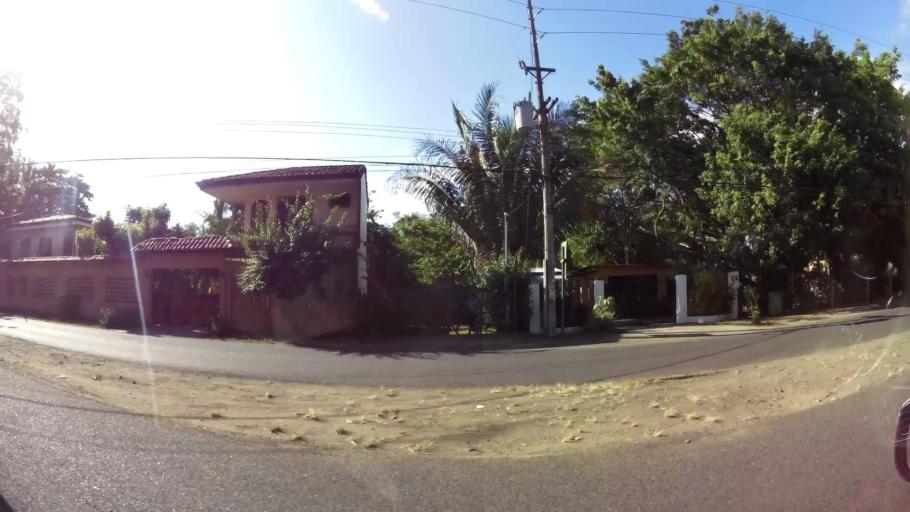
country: CR
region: Puntarenas
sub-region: Canton de Garabito
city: Jaco
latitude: 9.6232
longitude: -84.6369
